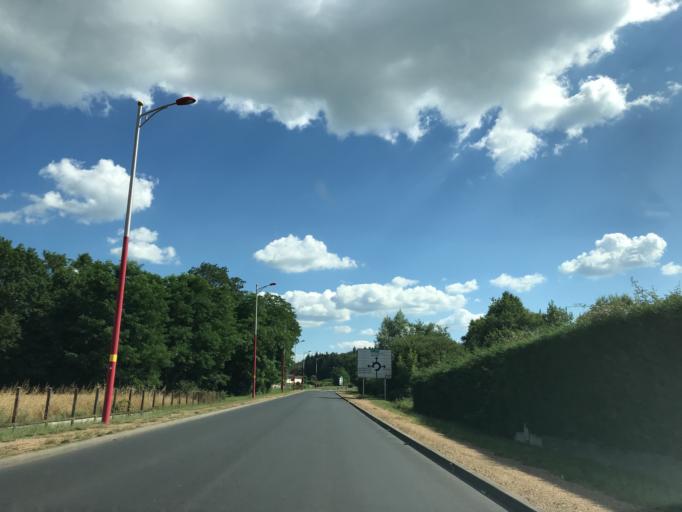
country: FR
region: Auvergne
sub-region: Departement du Puy-de-Dome
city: Courpiere
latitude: 45.7470
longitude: 3.5460
